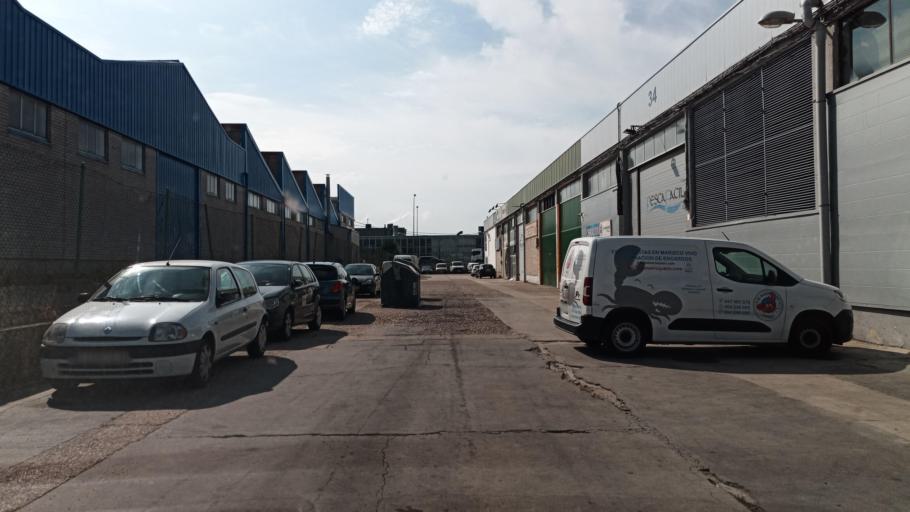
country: ES
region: Castille and Leon
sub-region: Provincia de Burgos
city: Burgos
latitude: 42.3587
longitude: -3.6548
